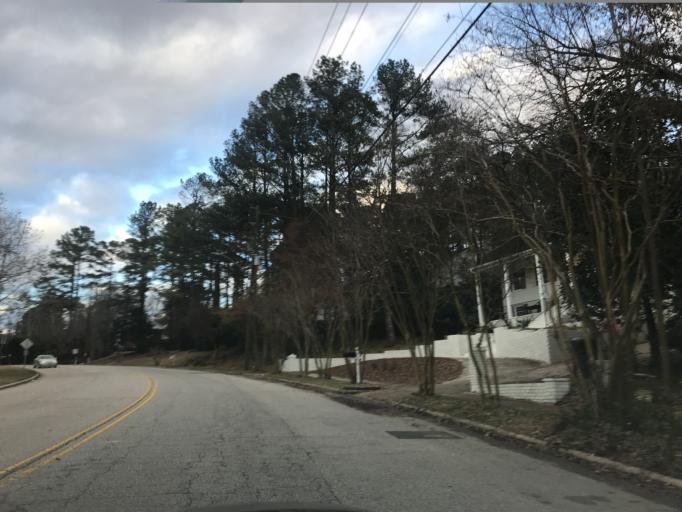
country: US
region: North Carolina
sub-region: Wake County
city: West Raleigh
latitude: 35.8427
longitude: -78.6617
